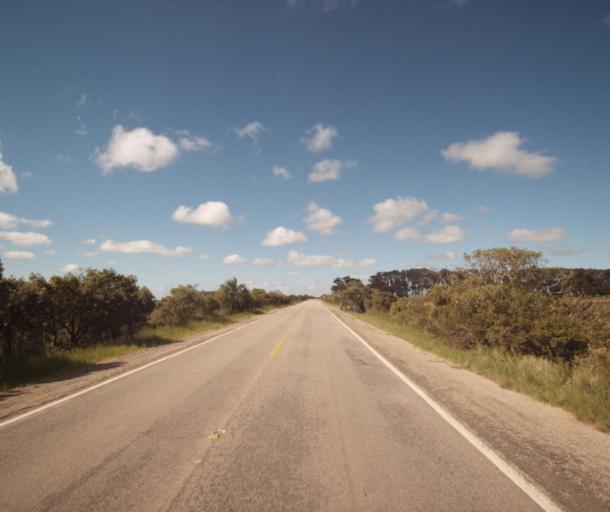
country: BR
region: Rio Grande do Sul
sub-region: Santa Vitoria Do Palmar
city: Santa Vitoria do Palmar
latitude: -33.4090
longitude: -53.2275
